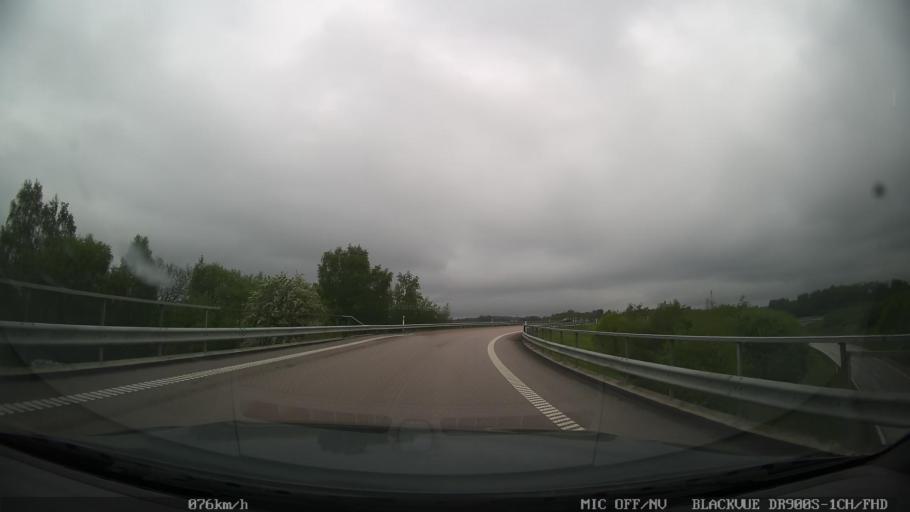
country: SE
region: Skane
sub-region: Helsingborg
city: Odakra
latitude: 56.0889
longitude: 12.7859
